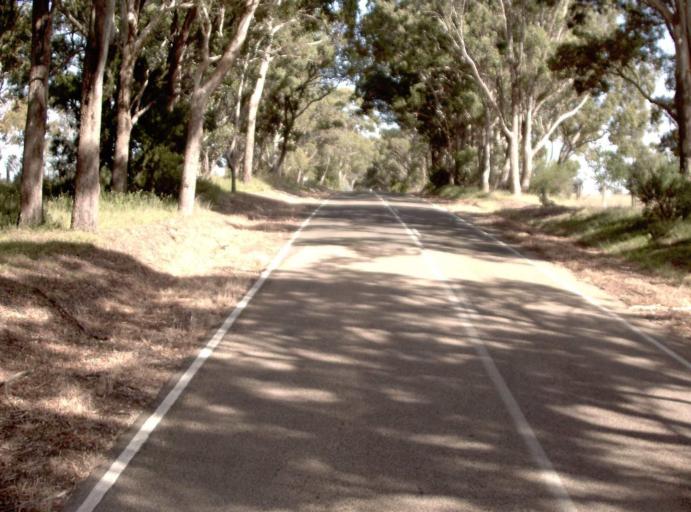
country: AU
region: Victoria
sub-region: East Gippsland
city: Lakes Entrance
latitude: -37.8134
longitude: 147.8478
